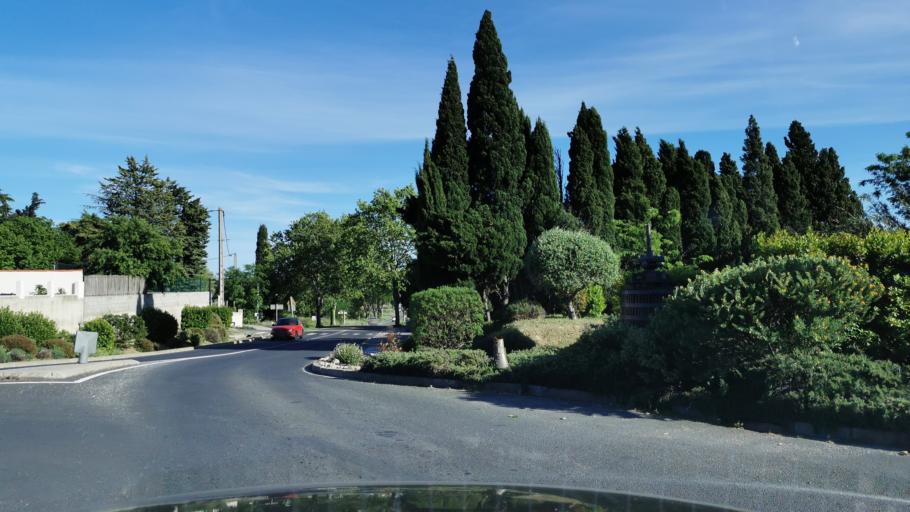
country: FR
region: Languedoc-Roussillon
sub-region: Departement de l'Aude
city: Marcorignan
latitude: 43.2227
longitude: 2.9240
